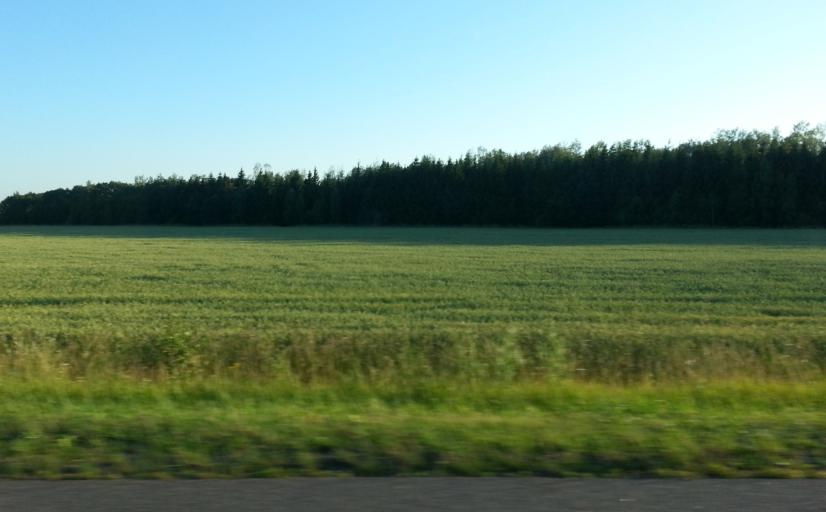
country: LT
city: Ramygala
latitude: 55.5414
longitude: 24.5347
